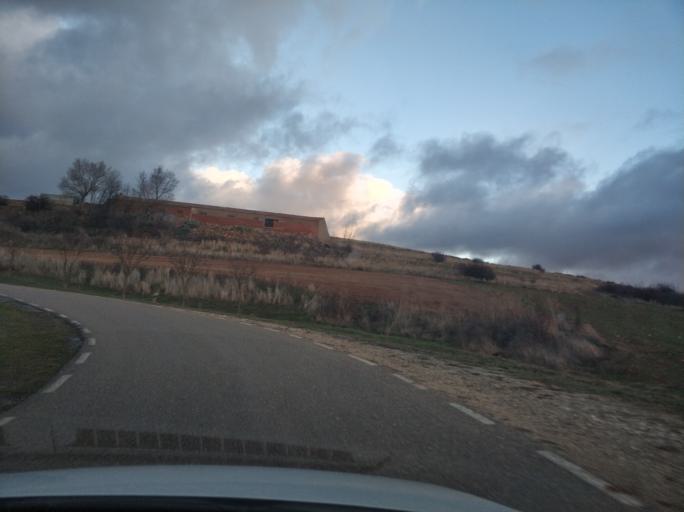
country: ES
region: Castille and Leon
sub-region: Provincia de Segovia
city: Ayllon
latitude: 41.4126
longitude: -3.4070
